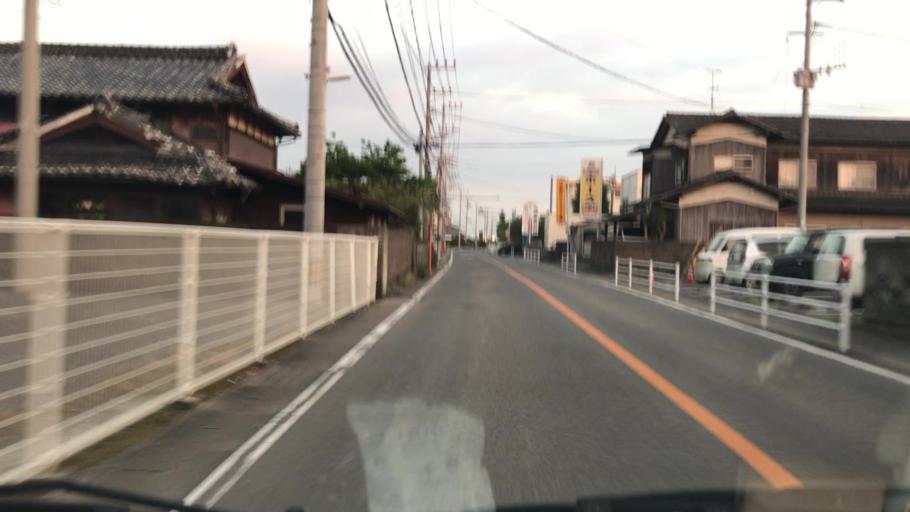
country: JP
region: Saga Prefecture
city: Saga-shi
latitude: 33.2422
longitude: 130.2581
